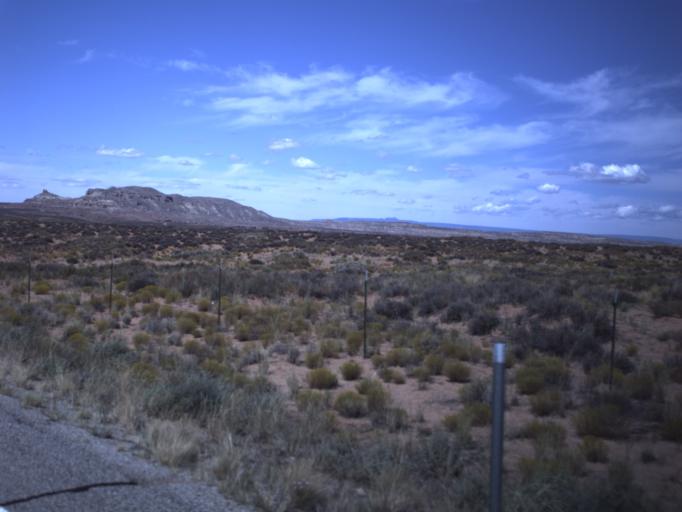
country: US
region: Utah
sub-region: San Juan County
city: Blanding
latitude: 37.3014
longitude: -109.4426
